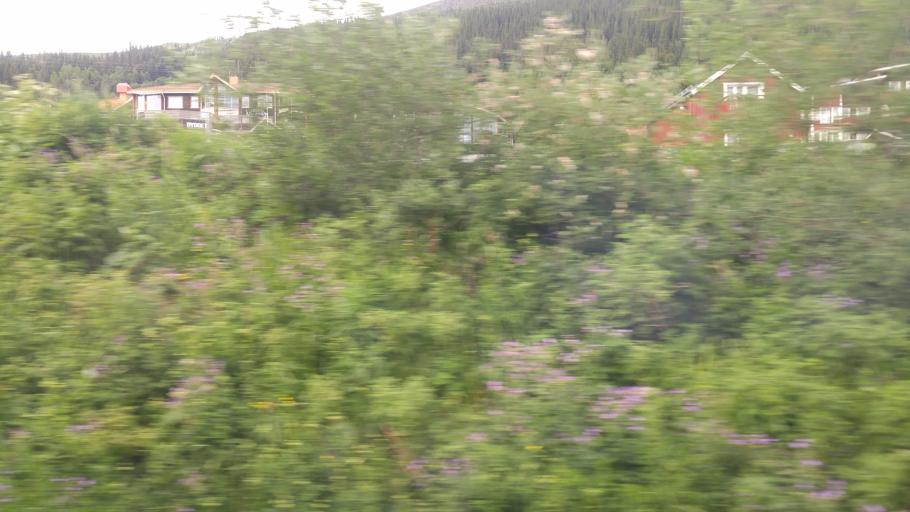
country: SE
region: Jaemtland
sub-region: Are Kommun
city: Are
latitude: 63.4023
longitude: 13.0636
